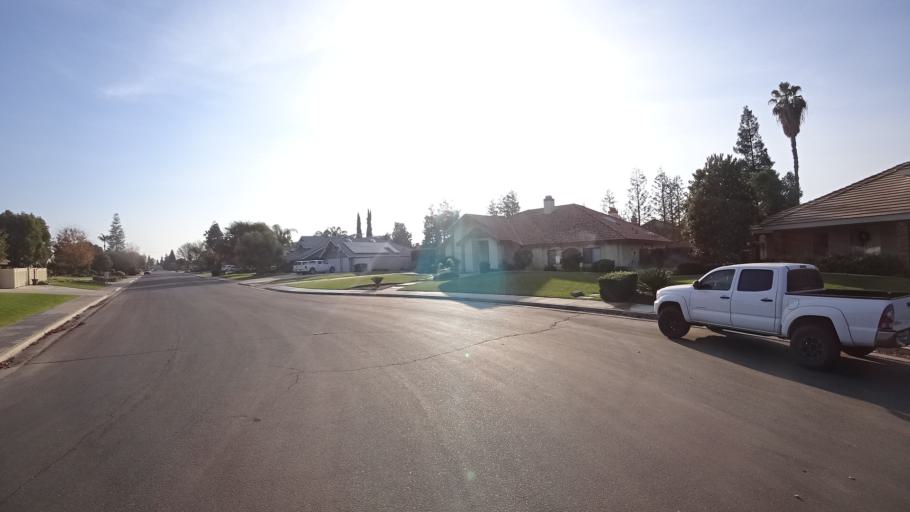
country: US
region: California
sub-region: Kern County
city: Rosedale
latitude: 35.3730
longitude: -119.1310
